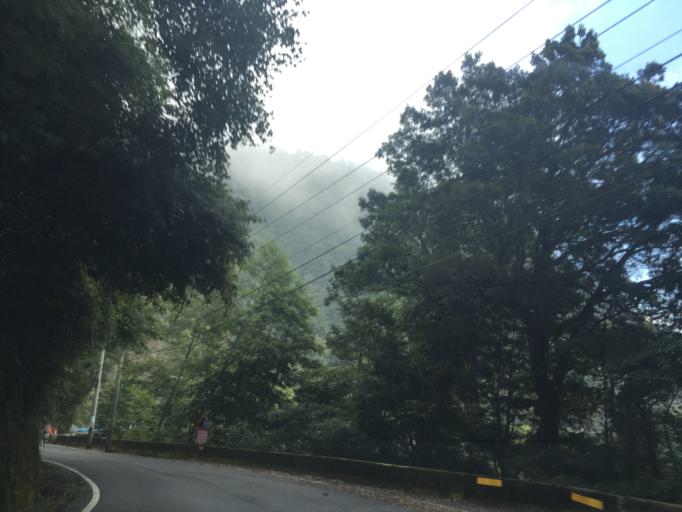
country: TW
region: Taiwan
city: Fengyuan
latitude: 24.2300
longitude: 120.9789
